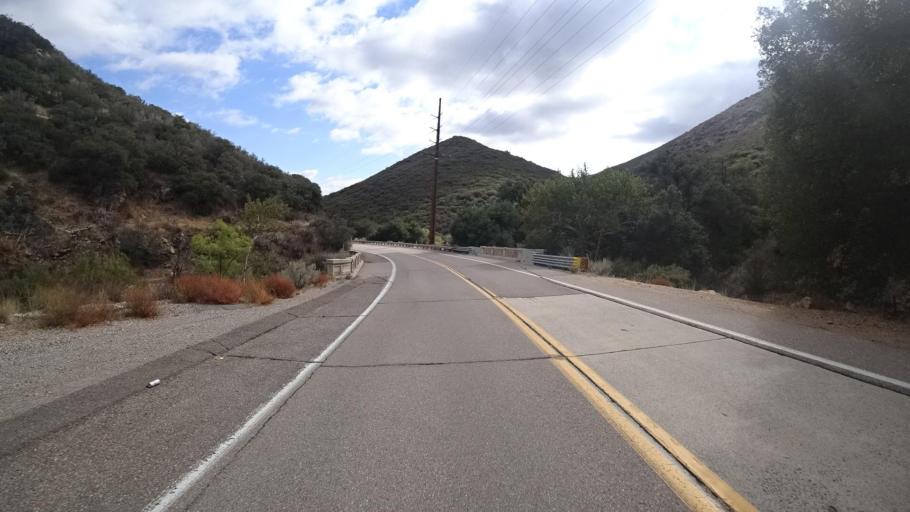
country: US
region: California
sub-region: San Diego County
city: Pine Valley
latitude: 32.7886
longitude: -116.4973
